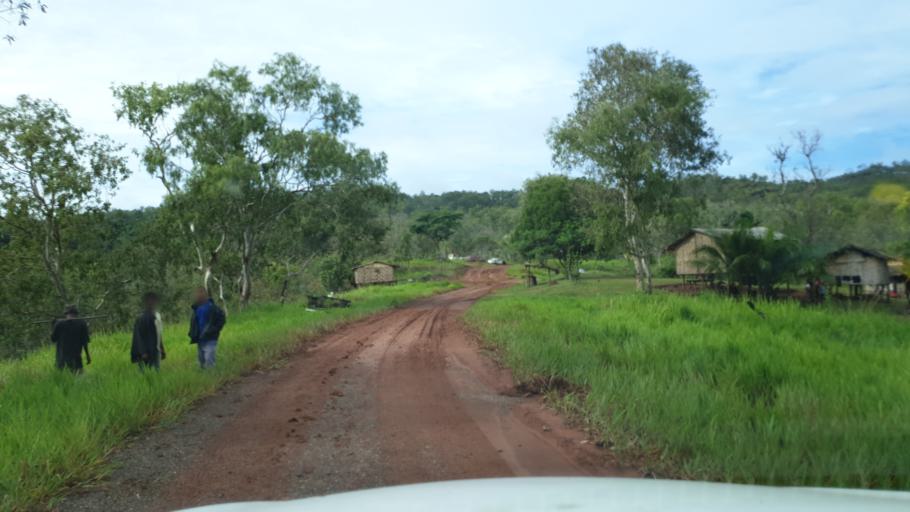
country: PG
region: National Capital
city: Port Moresby
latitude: -9.4349
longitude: 147.3967
